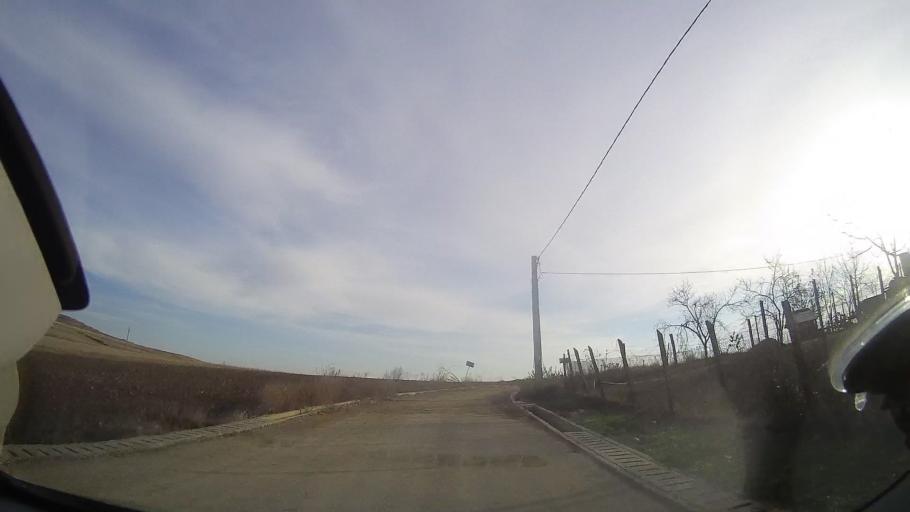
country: RO
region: Bihor
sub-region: Comuna Tileagd
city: Tileagd
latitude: 47.0998
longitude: 22.1763
